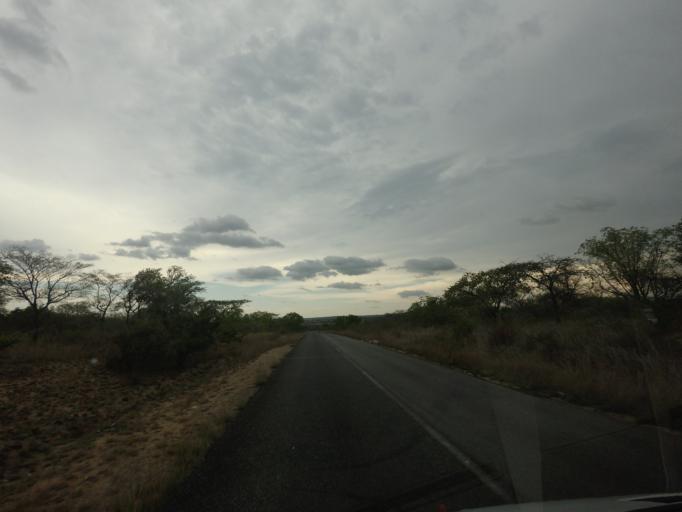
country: ZA
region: Limpopo
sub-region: Mopani District Municipality
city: Hoedspruit
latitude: -24.5347
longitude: 31.0019
